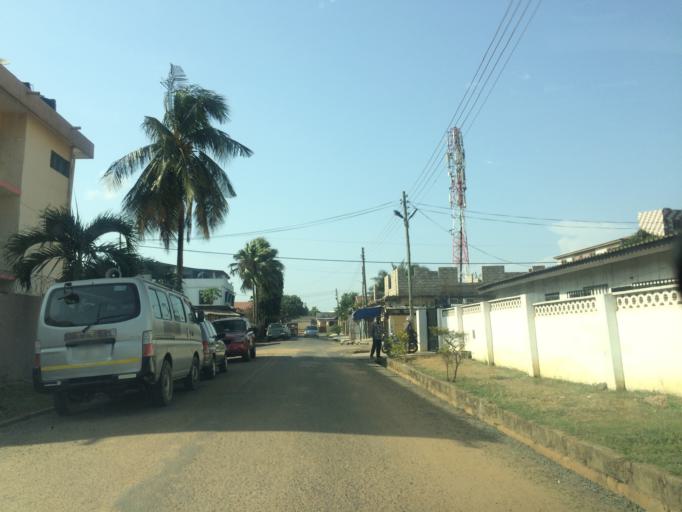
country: GH
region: Greater Accra
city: Accra
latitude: 5.5561
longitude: -0.1698
